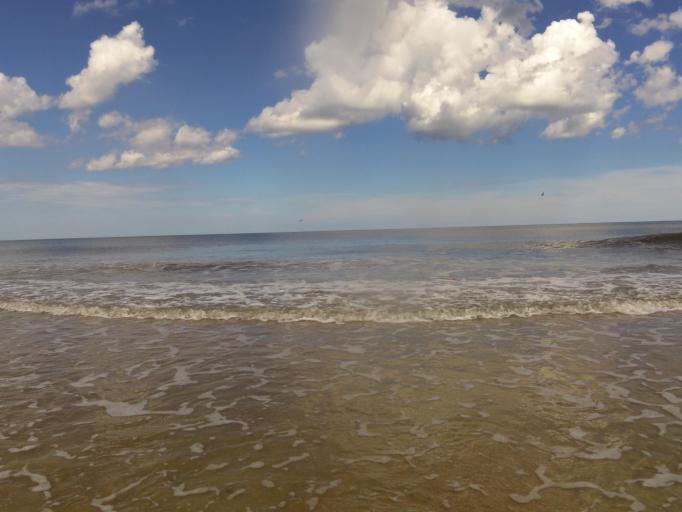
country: US
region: Florida
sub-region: Nassau County
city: Fernandina Beach
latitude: 30.6912
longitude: -81.4275
